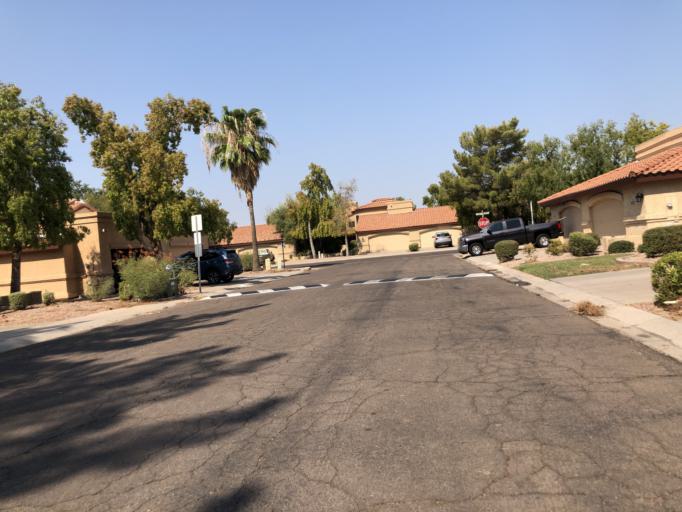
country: US
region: Arizona
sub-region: Maricopa County
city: Guadalupe
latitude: 33.3161
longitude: -111.9261
